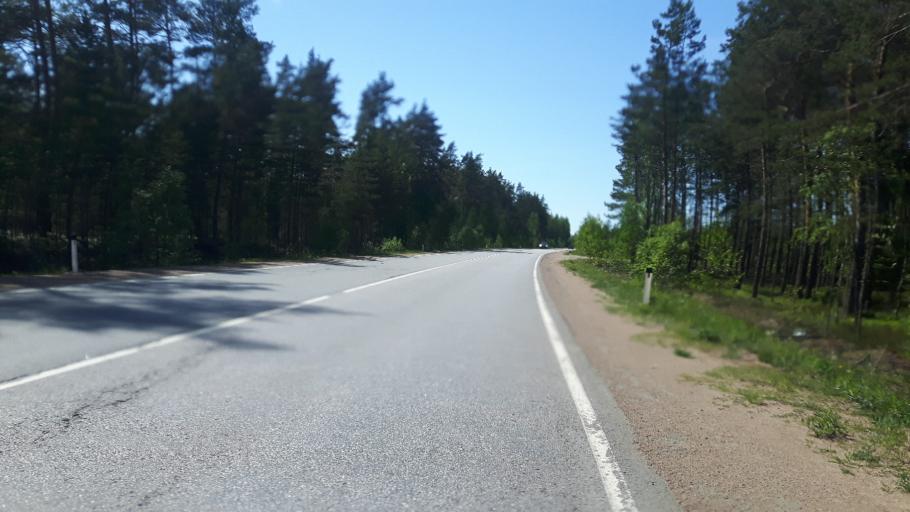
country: RU
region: Leningrad
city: Sista-Palkino
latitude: 59.7680
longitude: 28.7996
